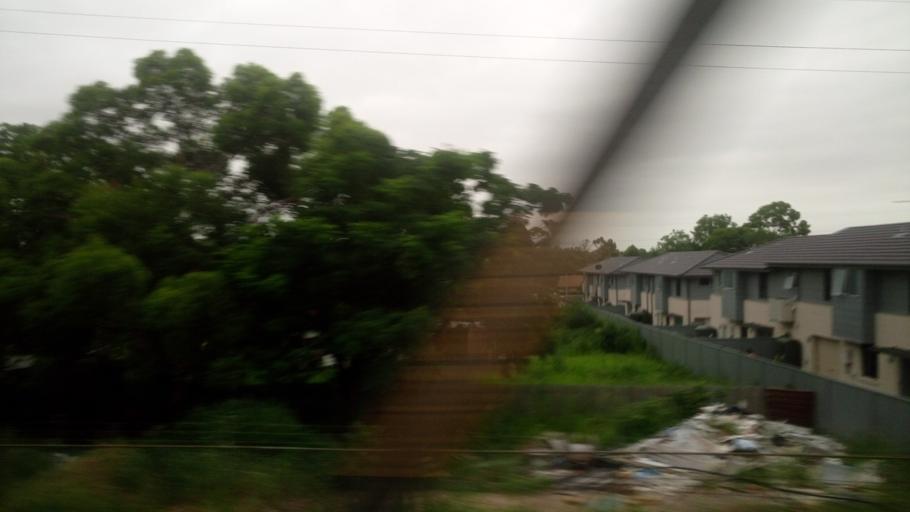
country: AU
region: New South Wales
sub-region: Penrith Municipality
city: Werrington County
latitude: -33.7579
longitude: 150.7504
